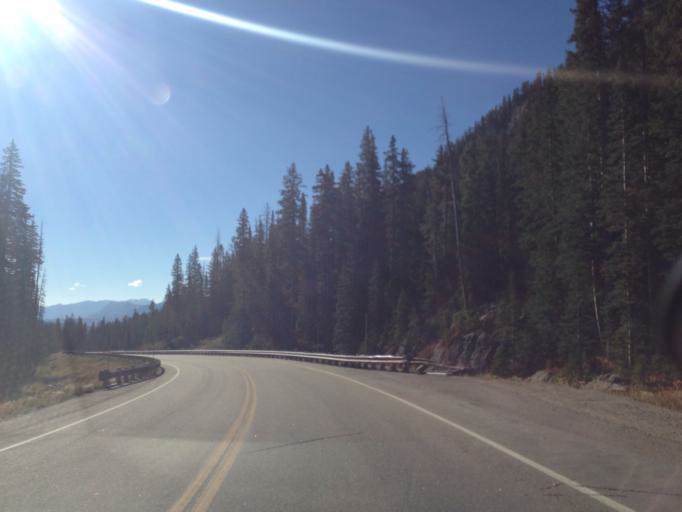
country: US
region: Montana
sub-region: Carbon County
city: Red Lodge
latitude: 45.0117
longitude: -109.8687
